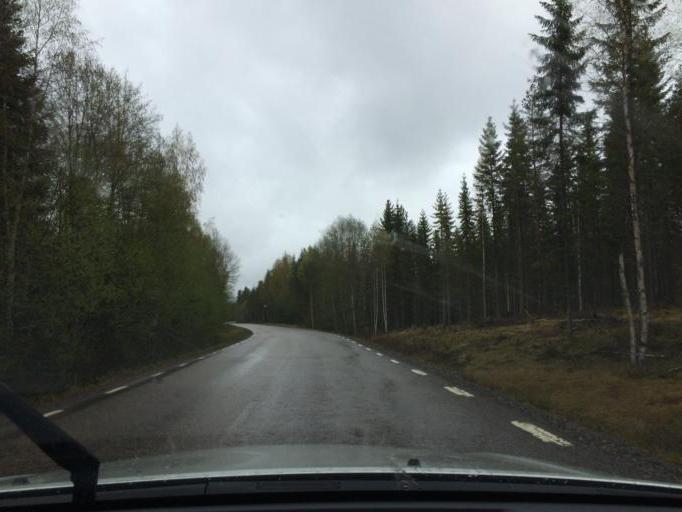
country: SE
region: Dalarna
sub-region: Ludvika Kommun
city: Abborrberget
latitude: 60.0633
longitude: 14.8454
